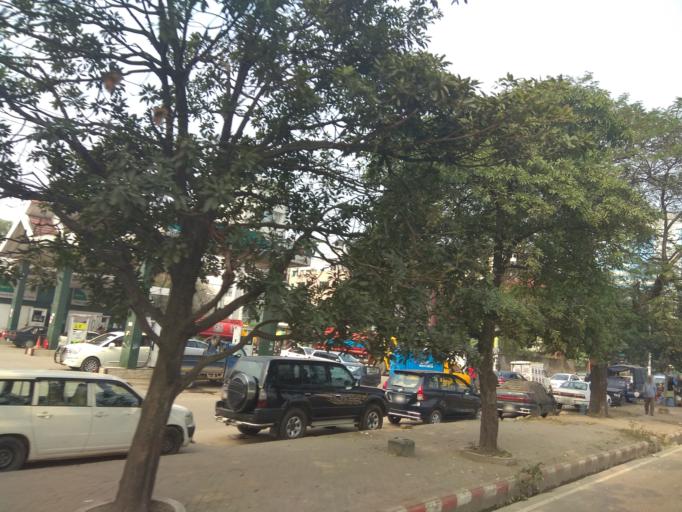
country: BD
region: Dhaka
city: Tungi
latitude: 23.8275
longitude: 90.4201
